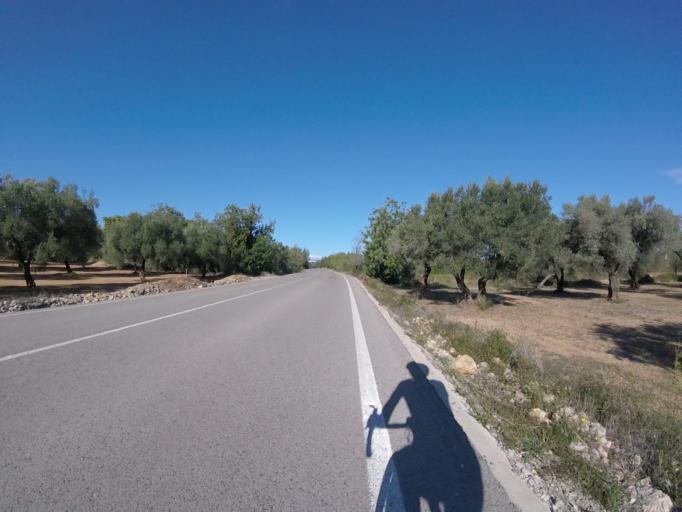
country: ES
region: Valencia
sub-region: Provincia de Castello
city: Cervera del Maestre
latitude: 40.4748
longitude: 0.2290
